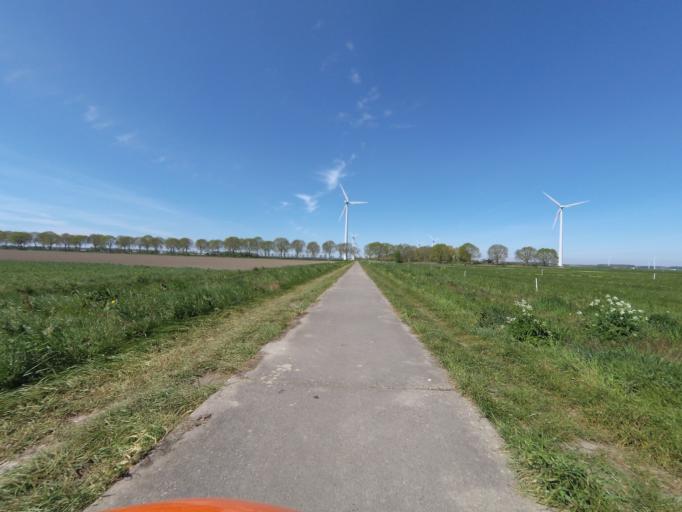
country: NL
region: Flevoland
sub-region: Gemeente Zeewolde
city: Zeewolde
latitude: 52.3752
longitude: 5.5101
